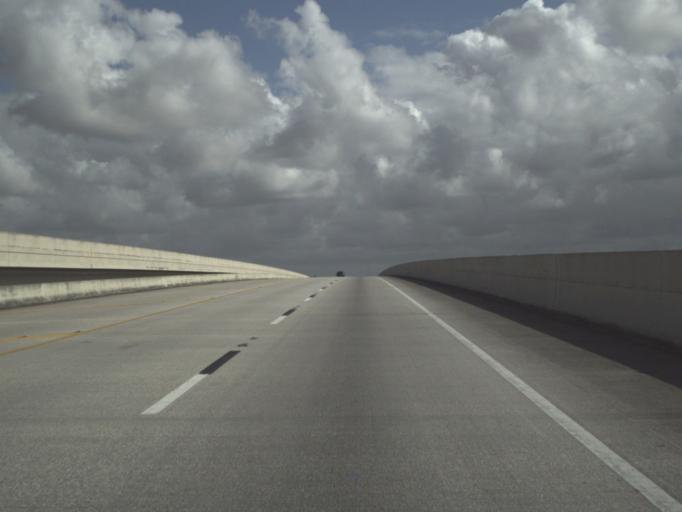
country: US
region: Florida
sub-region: Martin County
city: Palm City
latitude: 27.1196
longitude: -80.2763
